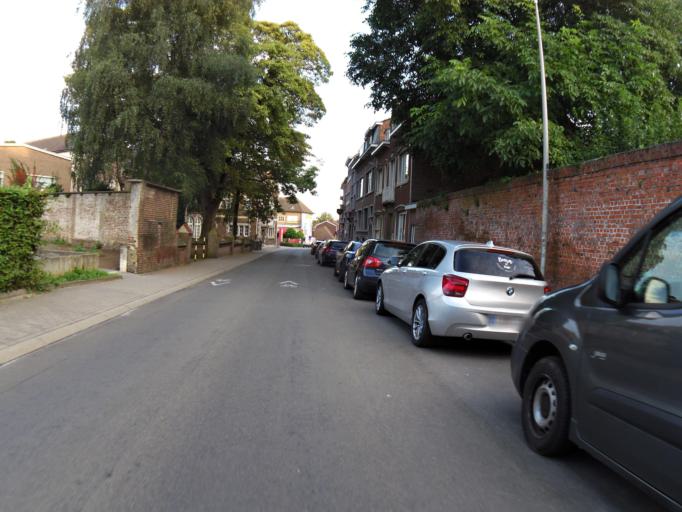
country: BE
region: Flanders
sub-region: Provincie Limburg
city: Tongeren
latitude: 50.7814
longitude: 5.4691
